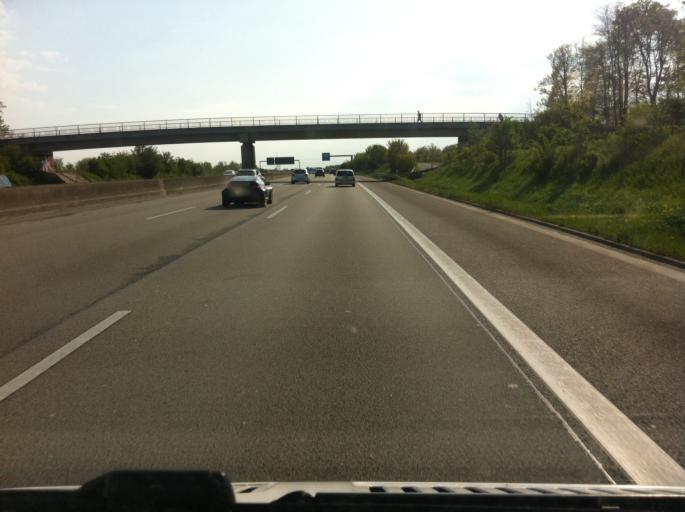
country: DE
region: Hesse
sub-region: Regierungsbezirk Darmstadt
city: Hattersheim
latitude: 50.0643
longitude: 8.4604
